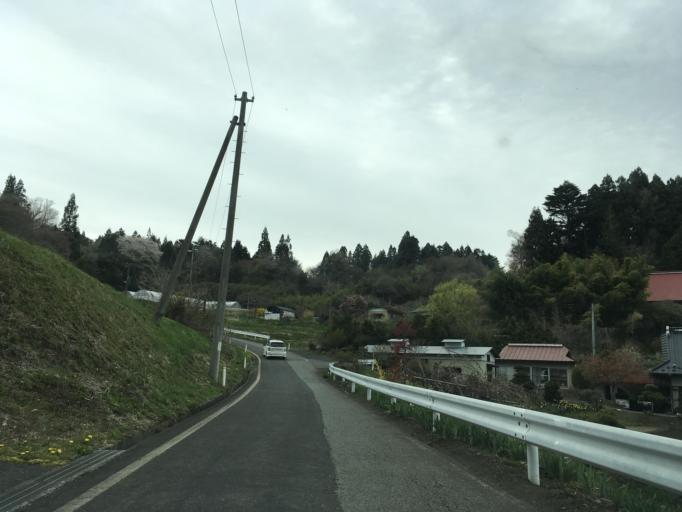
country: JP
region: Iwate
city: Ichinoseki
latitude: 38.8349
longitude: 141.3395
